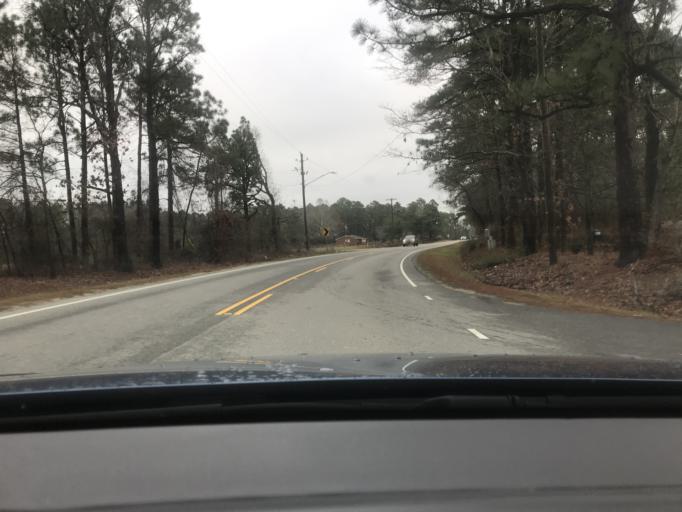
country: US
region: North Carolina
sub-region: Hoke County
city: Rockfish
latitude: 35.0264
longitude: -79.0116
